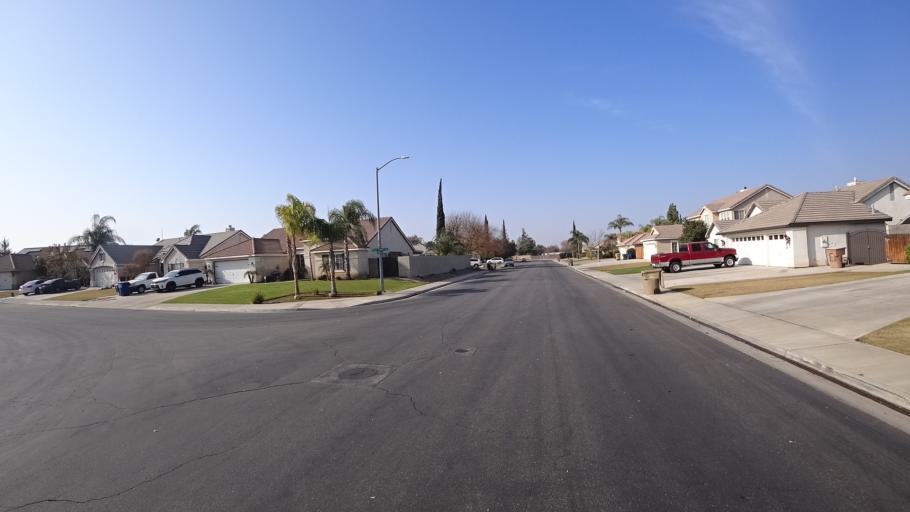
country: US
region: California
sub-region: Kern County
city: Greenacres
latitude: 35.4121
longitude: -119.1147
